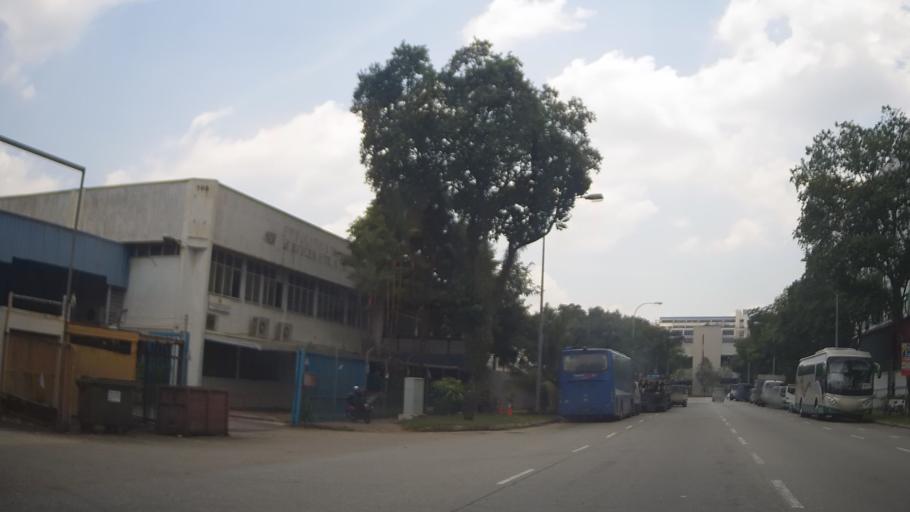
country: MY
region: Johor
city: Johor Bahru
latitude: 1.4534
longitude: 103.7966
